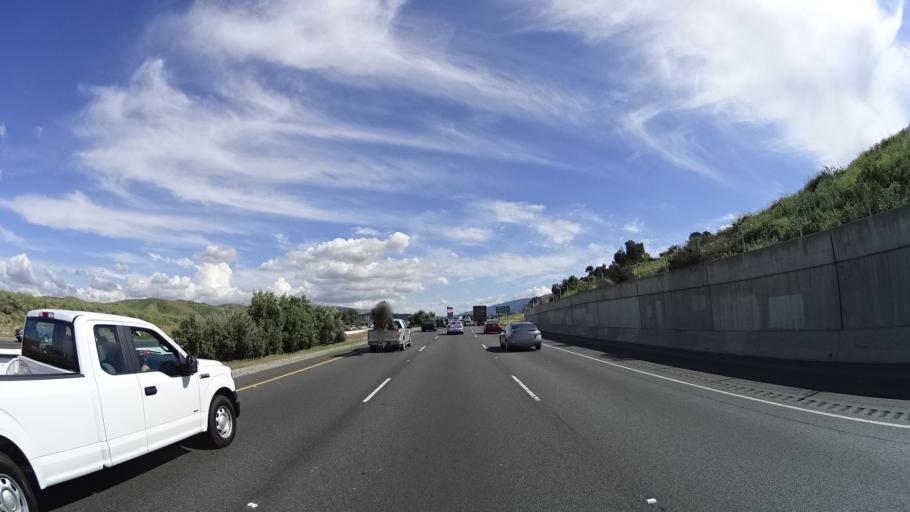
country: US
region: California
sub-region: Riverside County
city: El Cerrito
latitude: 33.8169
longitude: -117.5136
